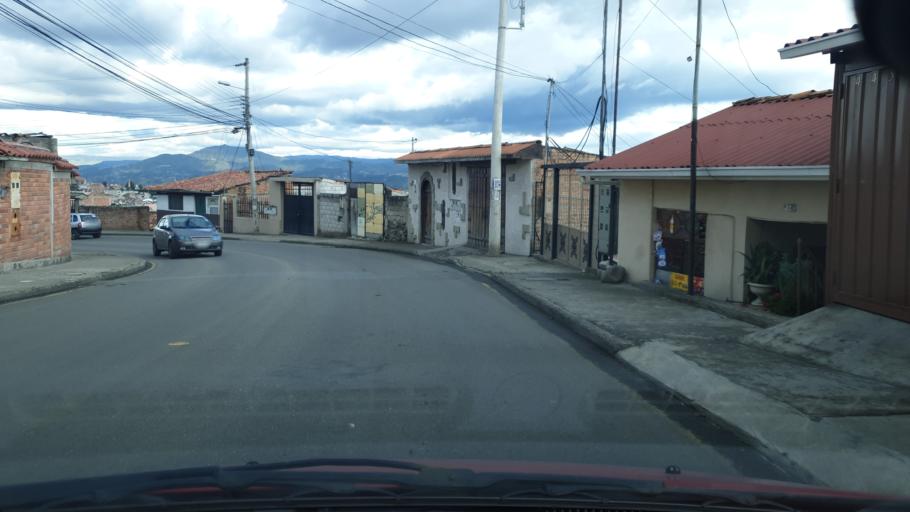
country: EC
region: Azuay
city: Cuenca
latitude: -2.8880
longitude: -79.0137
